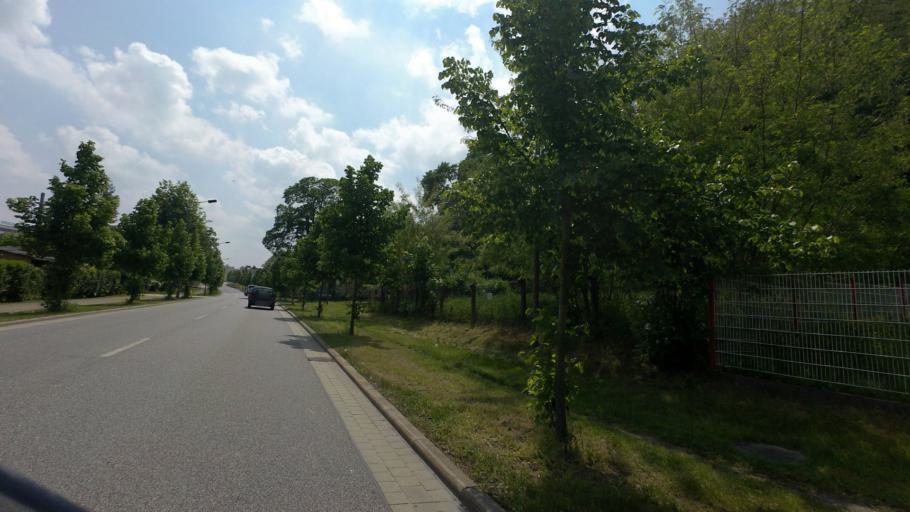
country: DE
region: Brandenburg
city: Spremberg
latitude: 51.5754
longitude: 14.3640
